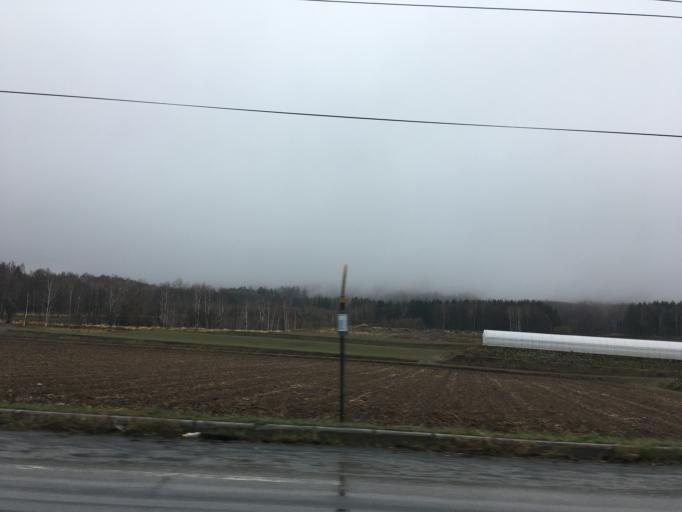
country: JP
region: Hokkaido
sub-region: Asahikawa-shi
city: Asahikawa
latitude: 43.9983
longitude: 142.4420
